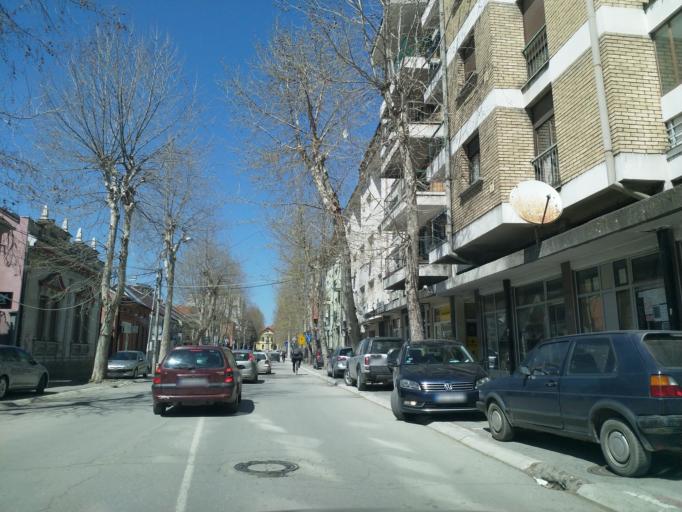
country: RS
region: Central Serbia
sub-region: Kolubarski Okrug
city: Valjevo
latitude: 44.2713
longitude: 19.8862
